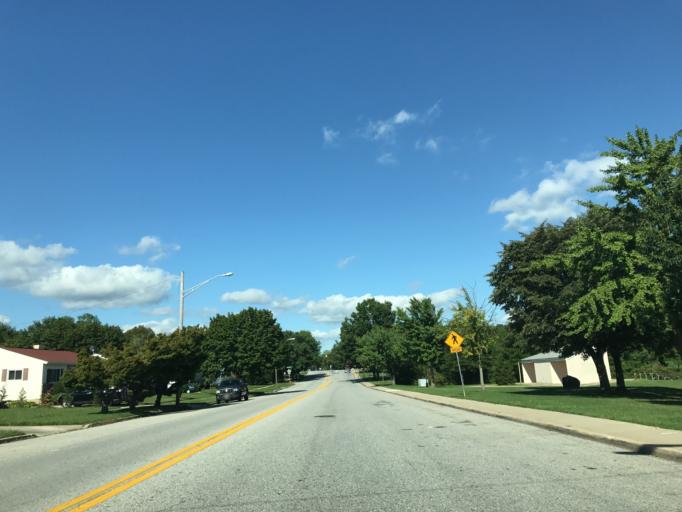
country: US
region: Maryland
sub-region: Baltimore County
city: Catonsville
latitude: 39.2981
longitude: -76.7506
